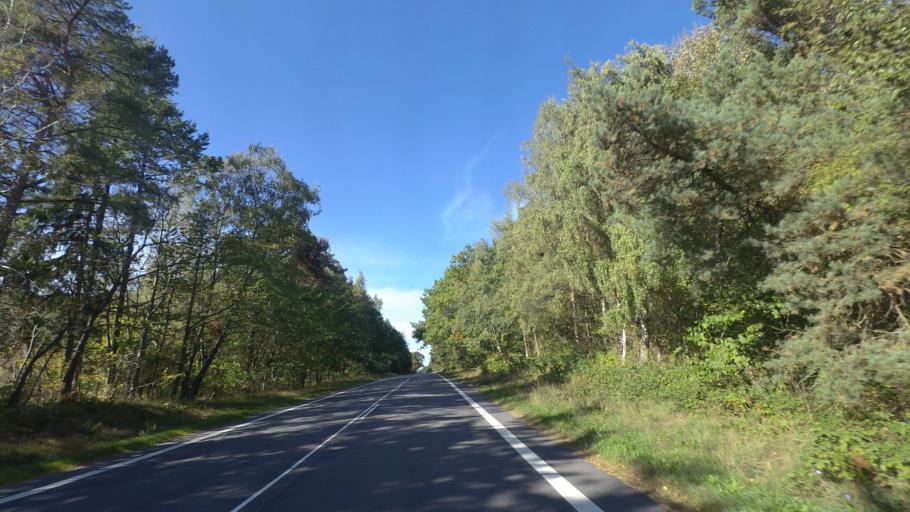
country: DK
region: Capital Region
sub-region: Bornholm Kommune
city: Ronne
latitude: 55.0824
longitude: 14.7521
